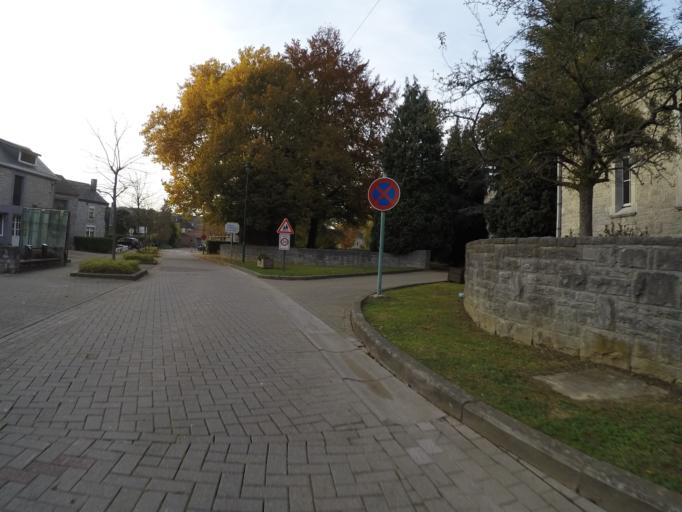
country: BE
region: Wallonia
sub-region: Province du Luxembourg
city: Hotton
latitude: 50.2681
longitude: 5.4456
